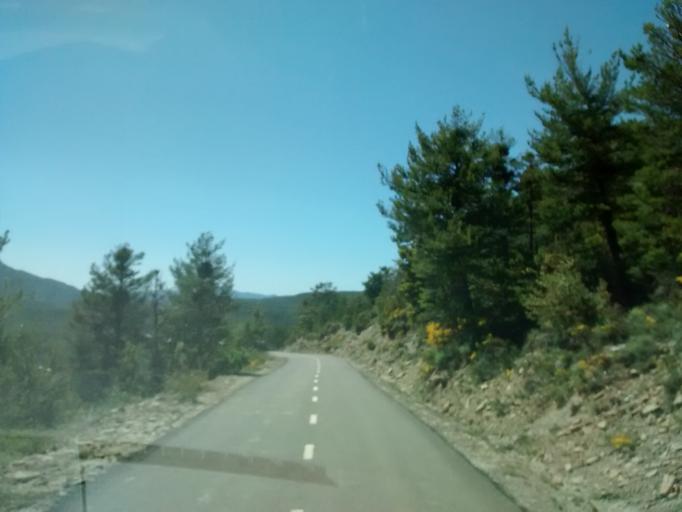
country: ES
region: Aragon
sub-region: Provincia de Huesca
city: Borau
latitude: 42.6730
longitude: -0.6094
